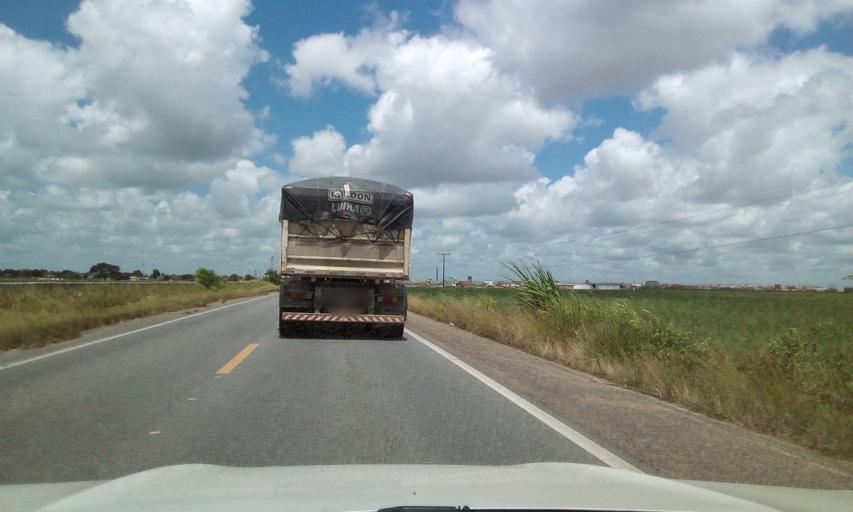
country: BR
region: Alagoas
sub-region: Sao Miguel Dos Campos
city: Sao Miguel dos Campos
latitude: -9.8154
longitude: -36.1204
